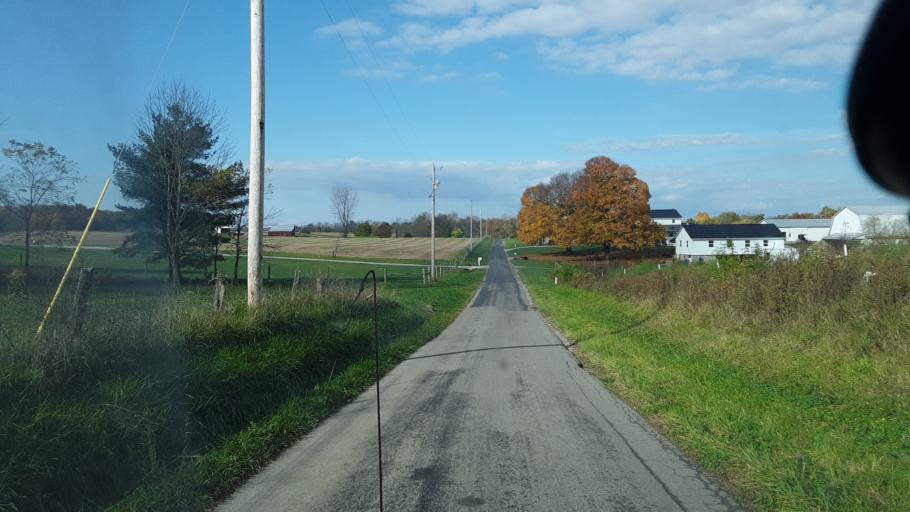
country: US
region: Ohio
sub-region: Highland County
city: Leesburg
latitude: 39.2855
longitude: -83.5385
